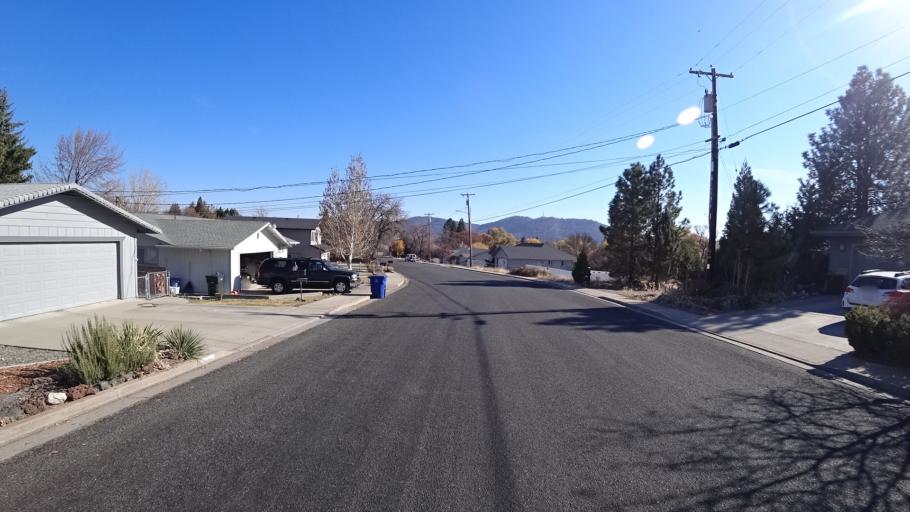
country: US
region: California
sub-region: Siskiyou County
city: Yreka
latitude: 41.7315
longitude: -122.6505
